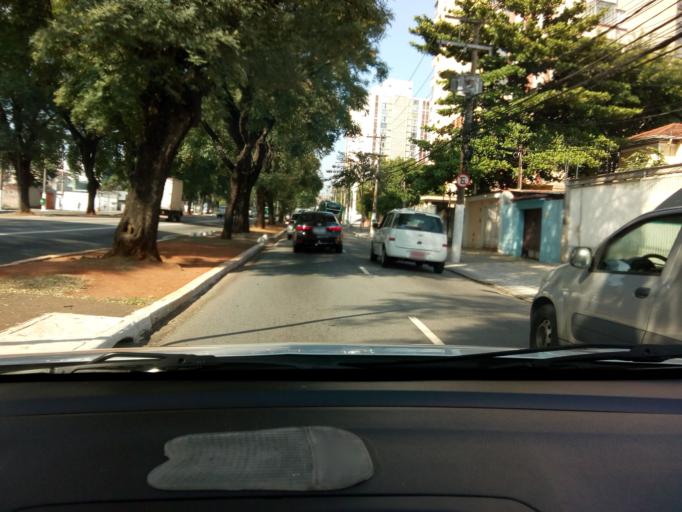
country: BR
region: Sao Paulo
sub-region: Sao Paulo
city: Sao Paulo
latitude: -23.5709
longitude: -46.6113
